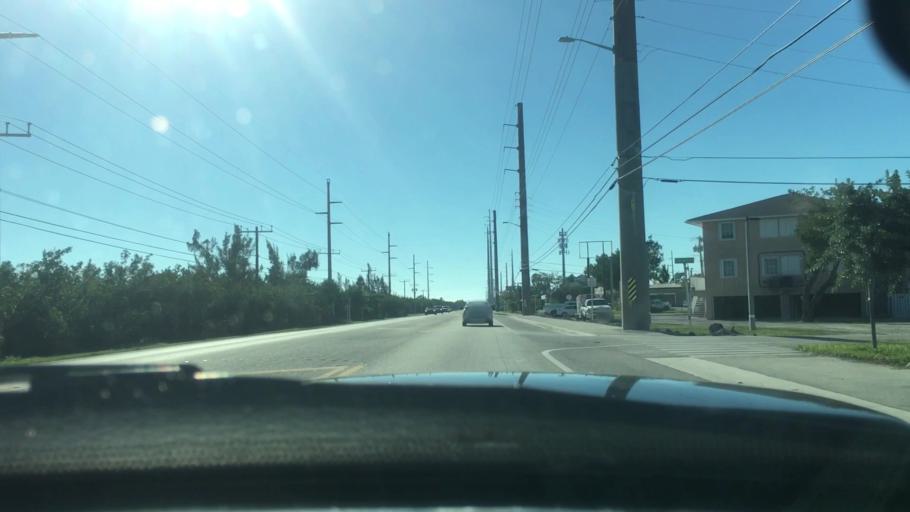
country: US
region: Florida
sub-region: Monroe County
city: Big Coppitt Key
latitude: 24.5975
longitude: -81.6559
